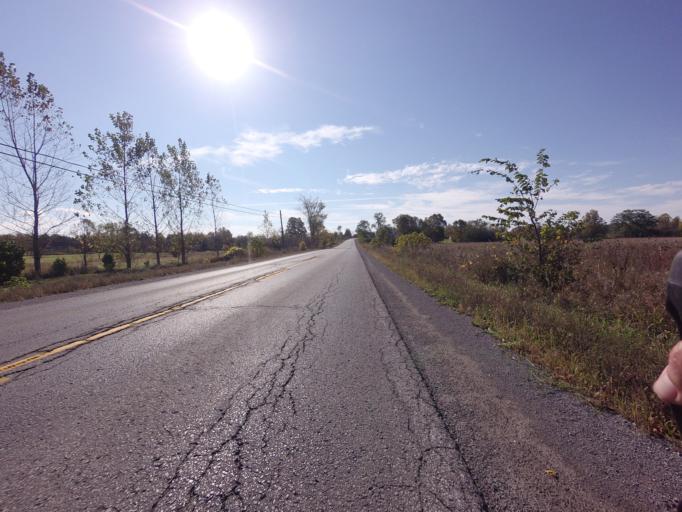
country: CA
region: Ontario
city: Prince Edward
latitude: 44.0151
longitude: -77.3640
